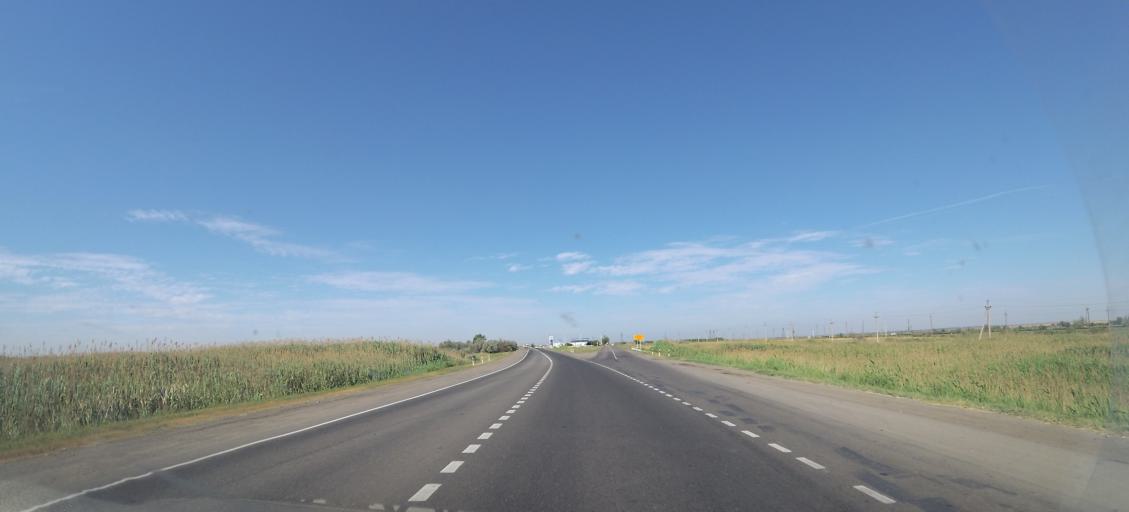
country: RU
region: Volgograd
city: Oktyabr'skiy
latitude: 48.6780
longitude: 43.8960
